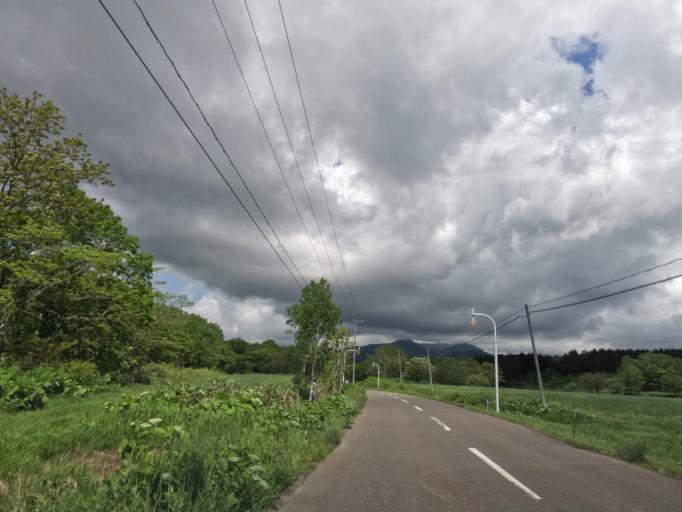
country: JP
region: Hokkaido
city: Tobetsu
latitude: 43.4508
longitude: 141.5889
